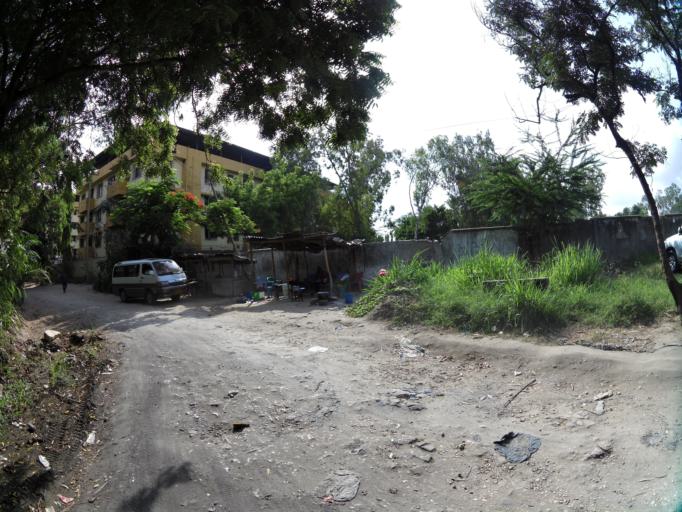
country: TZ
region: Dar es Salaam
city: Magomeni
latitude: -6.7701
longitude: 39.2478
